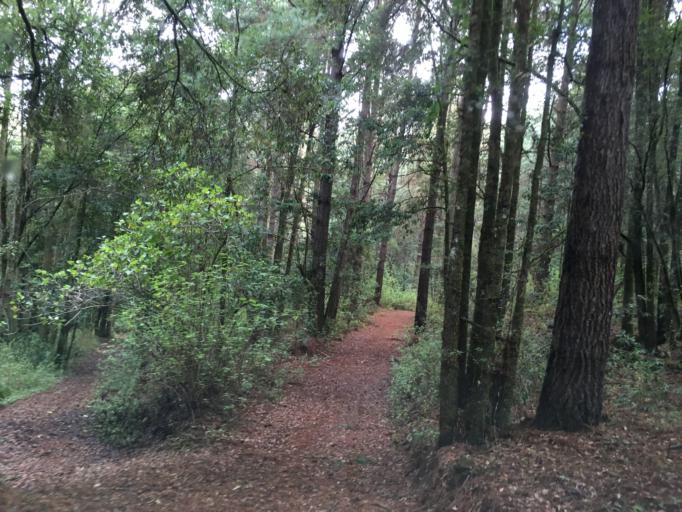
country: MX
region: Michoacan
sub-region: Zitacuaro
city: Francisco Serrato (San Bartolo)
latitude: 19.5195
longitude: -100.3062
